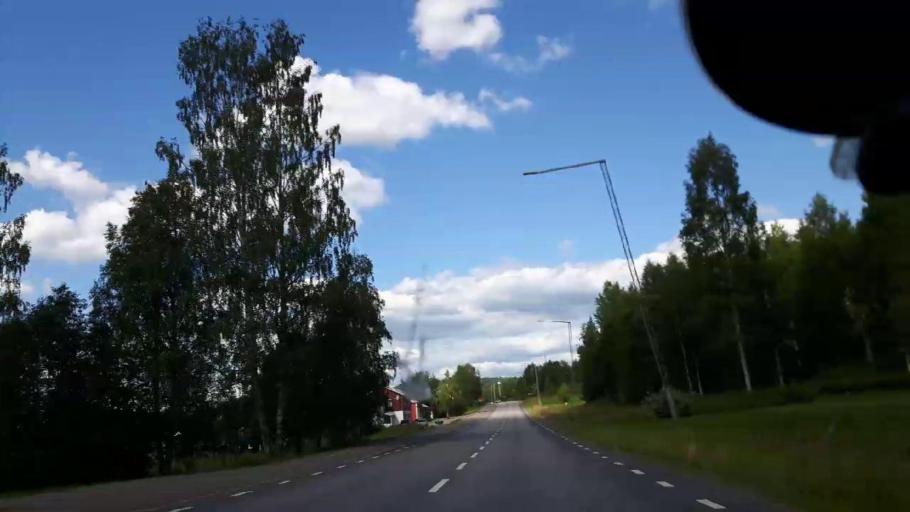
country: SE
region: Jaemtland
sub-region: Ragunda Kommun
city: Hammarstrand
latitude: 63.0067
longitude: 16.6667
